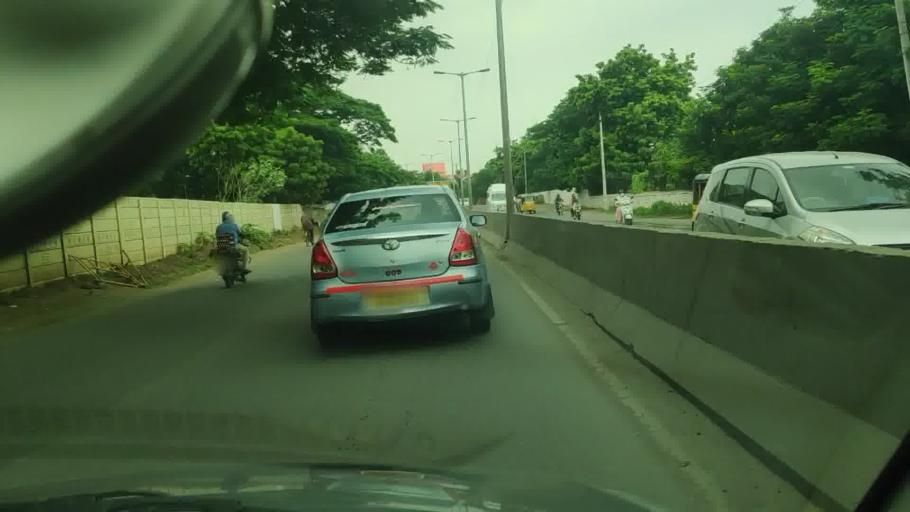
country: IN
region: Tamil Nadu
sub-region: Thiruvallur
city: Ambattur
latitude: 13.1173
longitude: 80.1491
